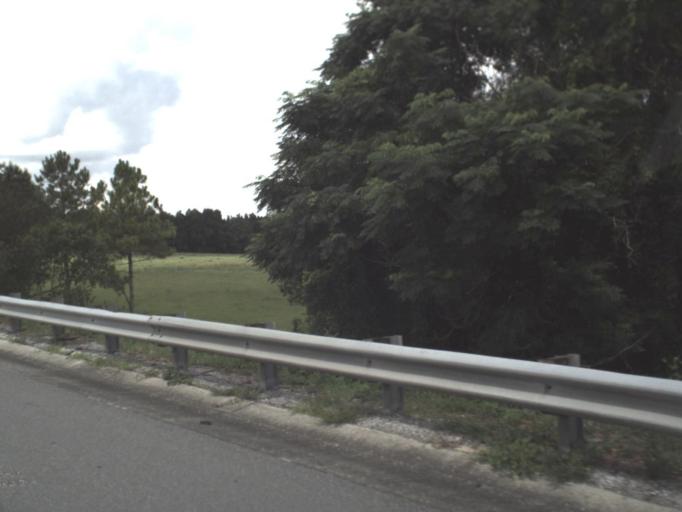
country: US
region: Florida
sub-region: Hernando County
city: Hill 'n Dale
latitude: 28.4850
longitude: -82.2490
